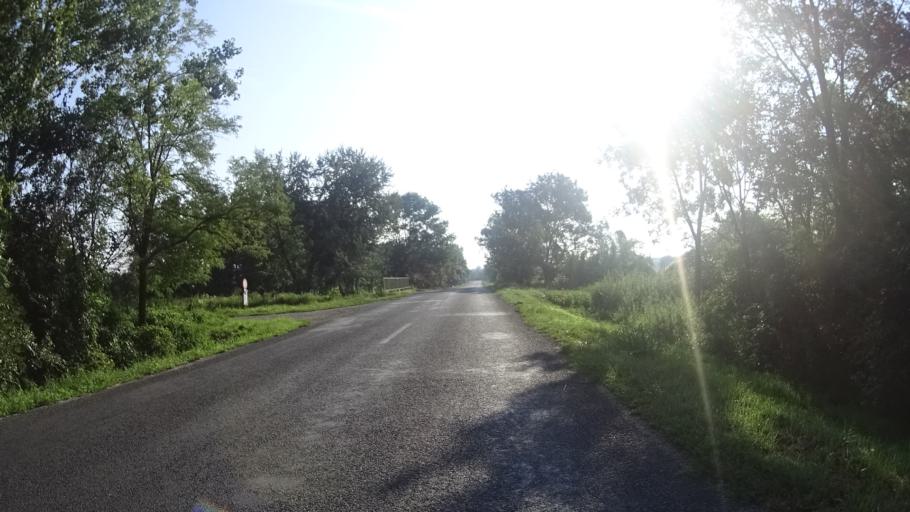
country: HU
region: Zala
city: Sarmellek
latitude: 46.6627
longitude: 17.1408
